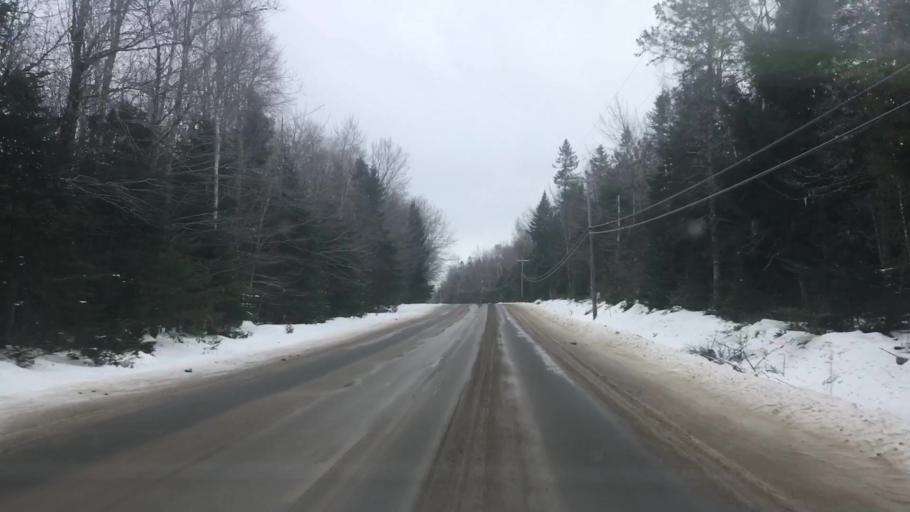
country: US
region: Maine
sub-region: Washington County
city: East Machias
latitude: 44.9910
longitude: -67.4605
